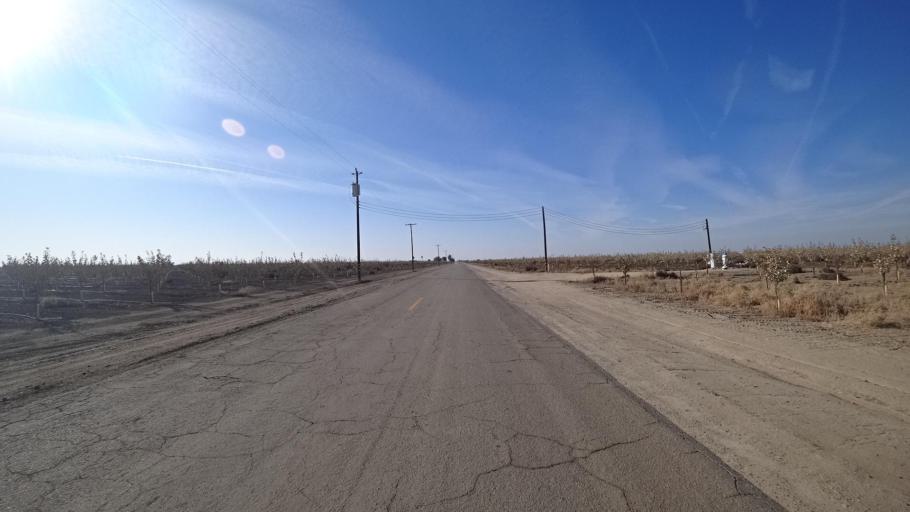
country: US
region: California
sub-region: Kern County
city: Wasco
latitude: 35.7032
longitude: -119.4110
